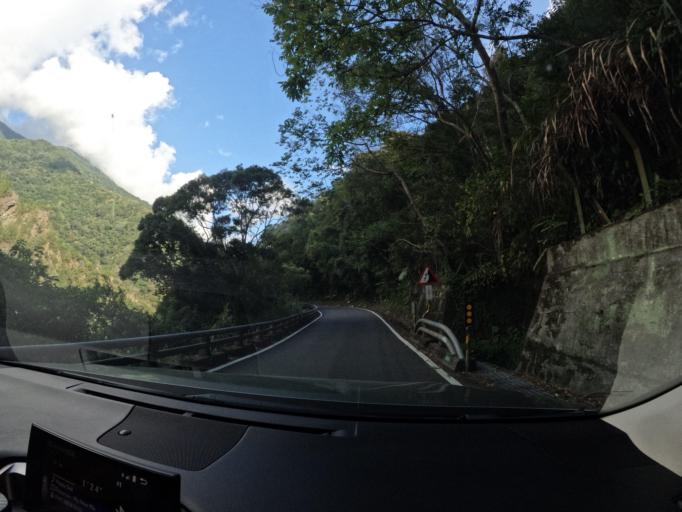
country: TW
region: Taiwan
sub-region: Taitung
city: Taitung
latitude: 23.1727
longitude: 121.0420
